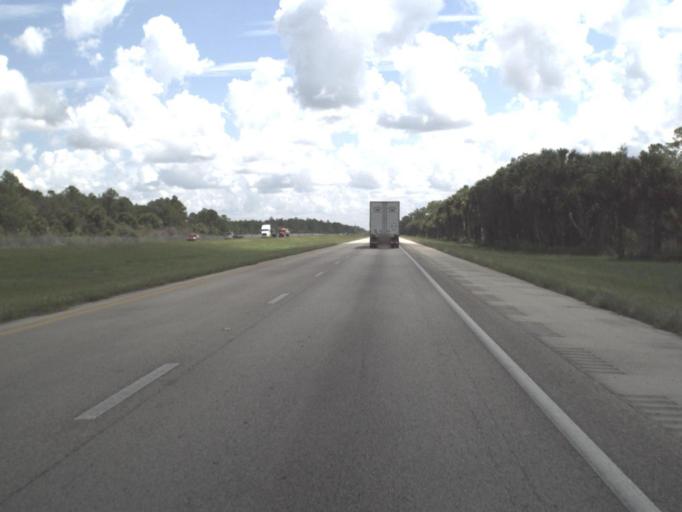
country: US
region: Florida
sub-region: Collier County
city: Orangetree
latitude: 26.1530
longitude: -81.4838
